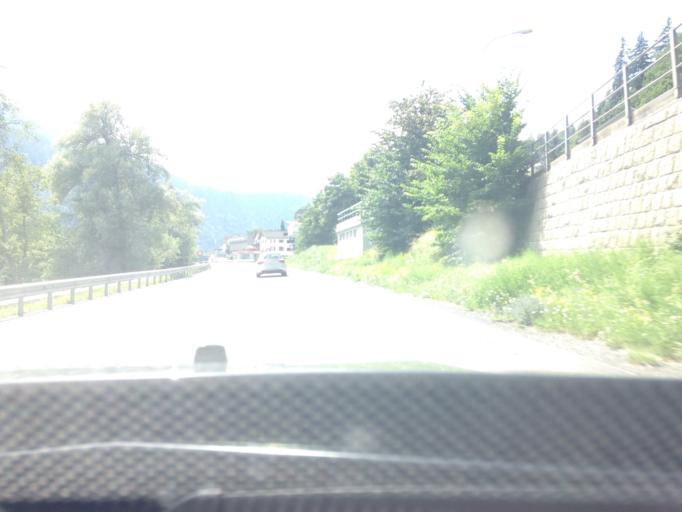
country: CH
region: Grisons
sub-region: Surselva District
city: Ilanz
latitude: 46.7770
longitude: 9.2091
